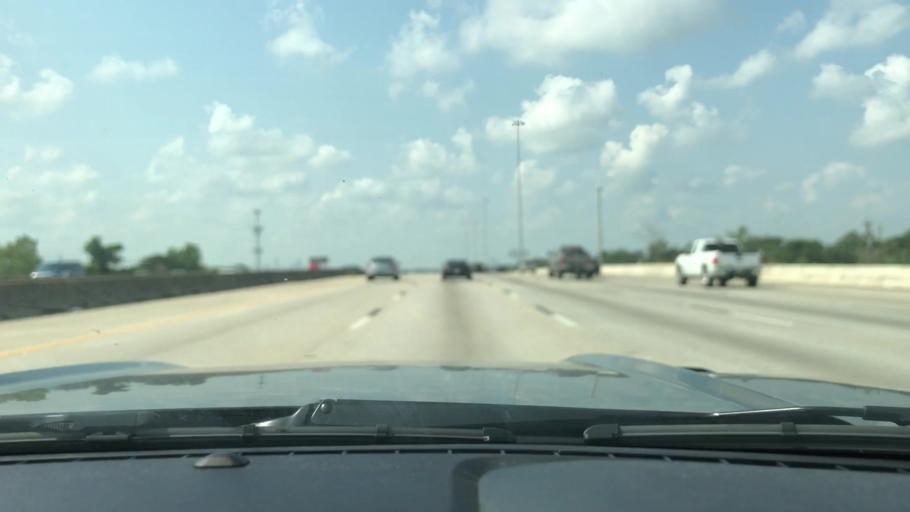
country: US
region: Texas
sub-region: Harris County
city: Aldine
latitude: 29.8805
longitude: -95.3243
